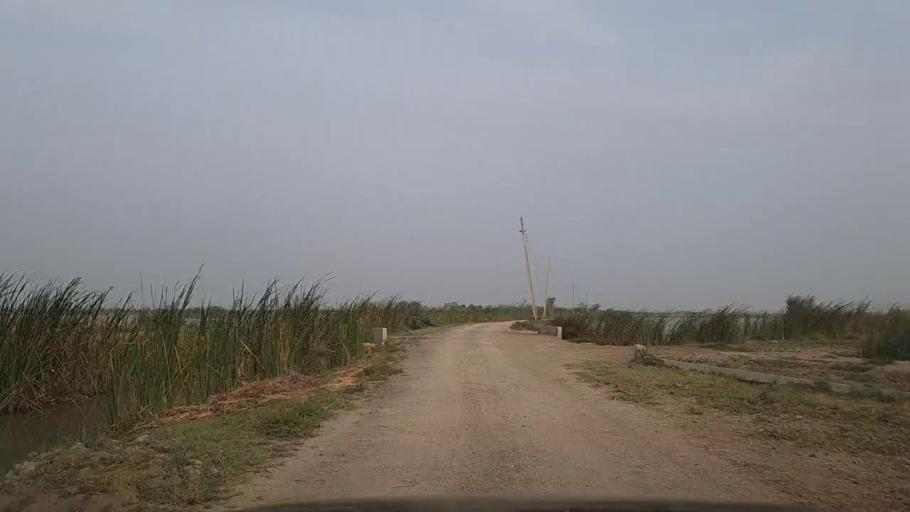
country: PK
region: Sindh
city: Chuhar Jamali
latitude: 24.5042
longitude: 67.8880
